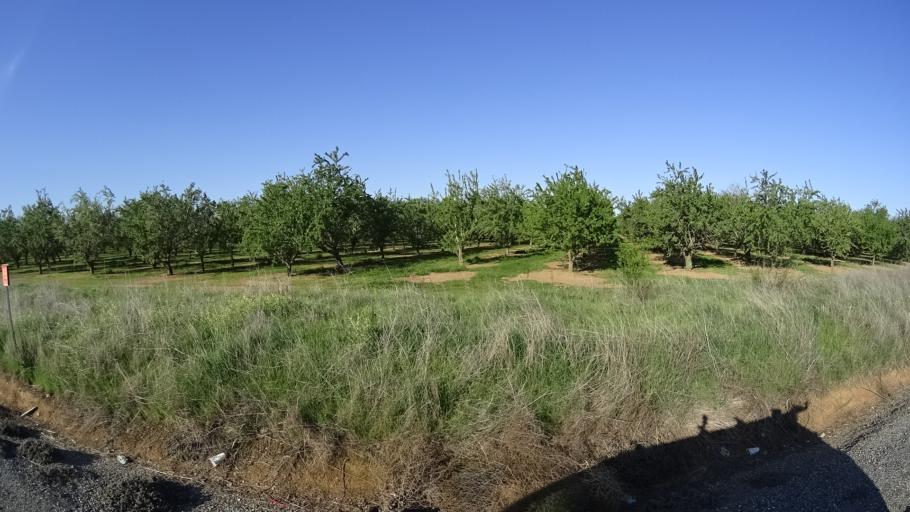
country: US
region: California
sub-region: Glenn County
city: Orland
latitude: 39.7962
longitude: -122.1242
